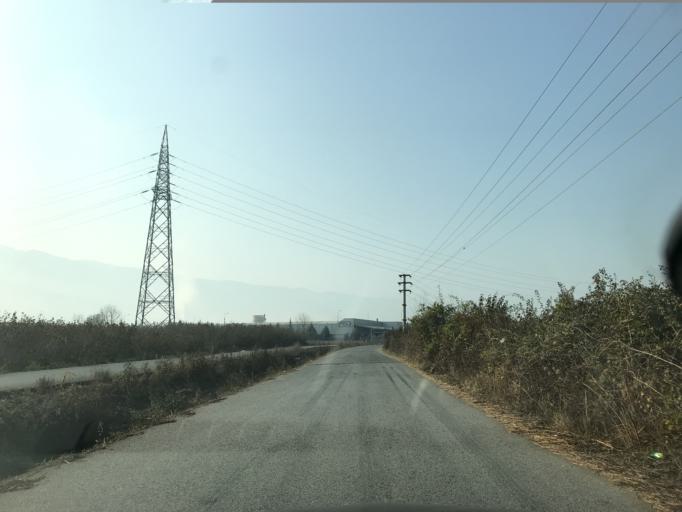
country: TR
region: Duzce
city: Duzce
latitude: 40.7900
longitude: 31.1547
